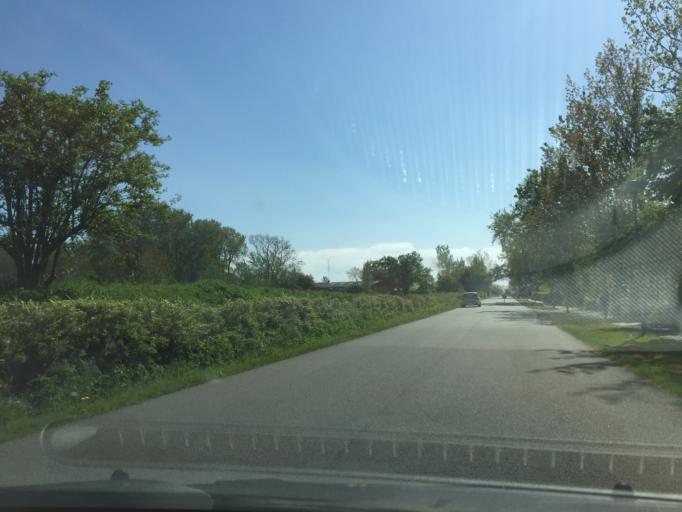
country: DK
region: Zealand
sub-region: Lolland Kommune
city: Rodbyhavn
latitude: 54.6704
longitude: 11.3388
